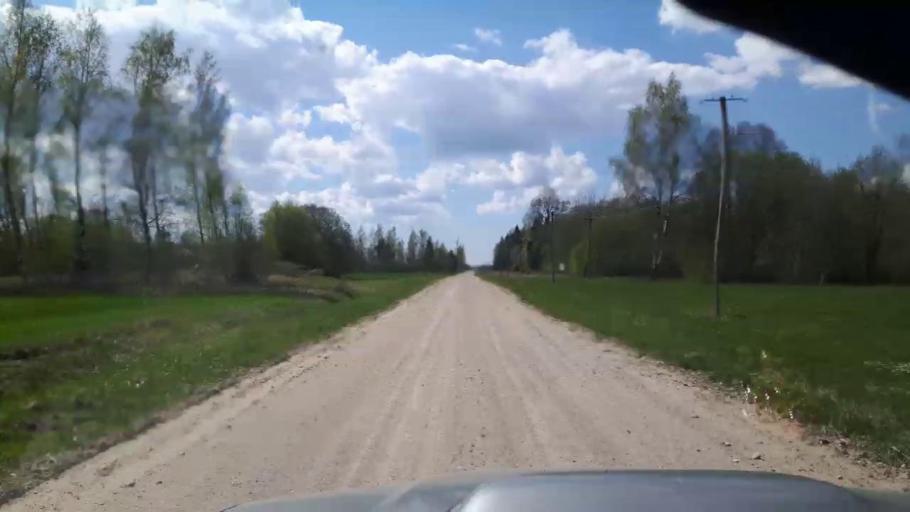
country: EE
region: Paernumaa
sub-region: Tootsi vald
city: Tootsi
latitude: 58.4696
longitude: 24.8973
